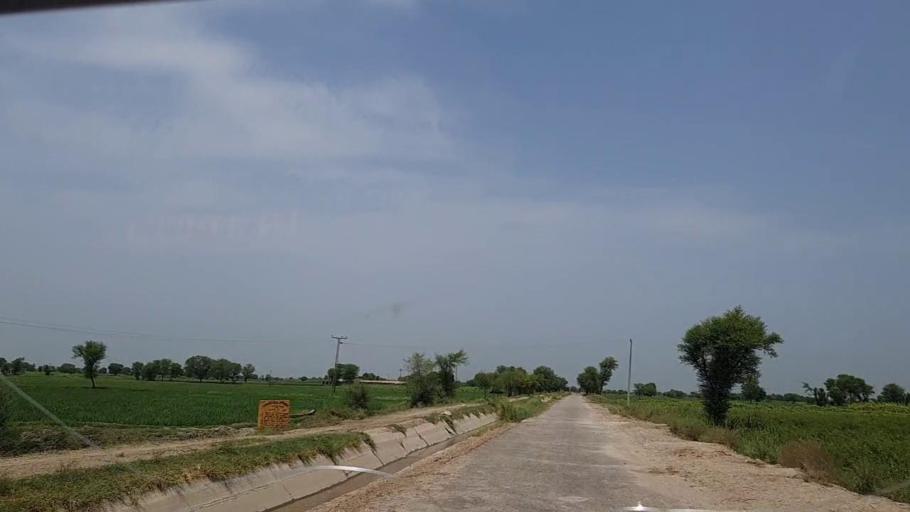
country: PK
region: Sindh
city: Tharu Shah
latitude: 26.9334
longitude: 68.0683
